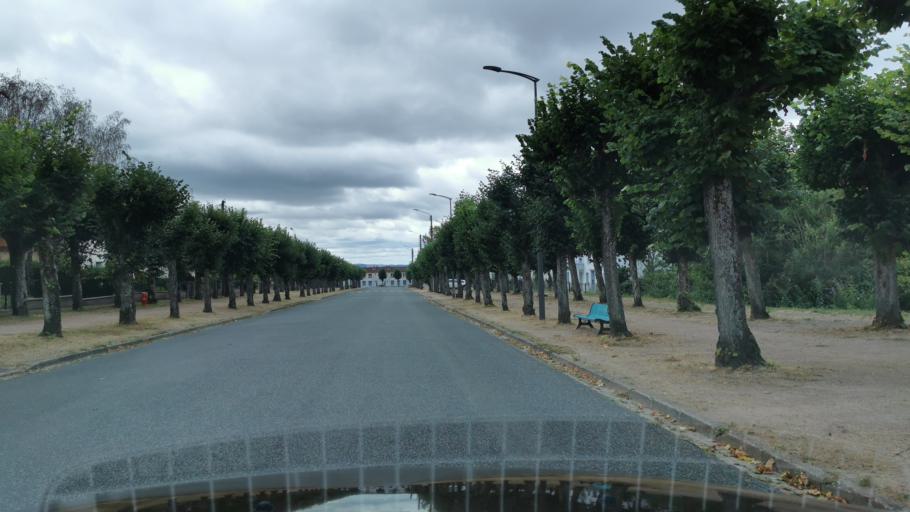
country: FR
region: Bourgogne
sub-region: Departement de Saone-et-Loire
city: Le Breuil
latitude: 46.8077
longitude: 4.4449
